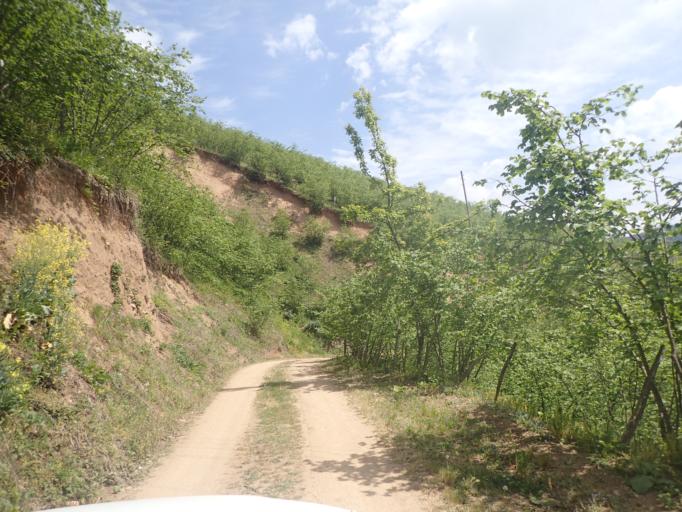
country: TR
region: Ordu
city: Kabaduz
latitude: 40.7982
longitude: 37.8873
